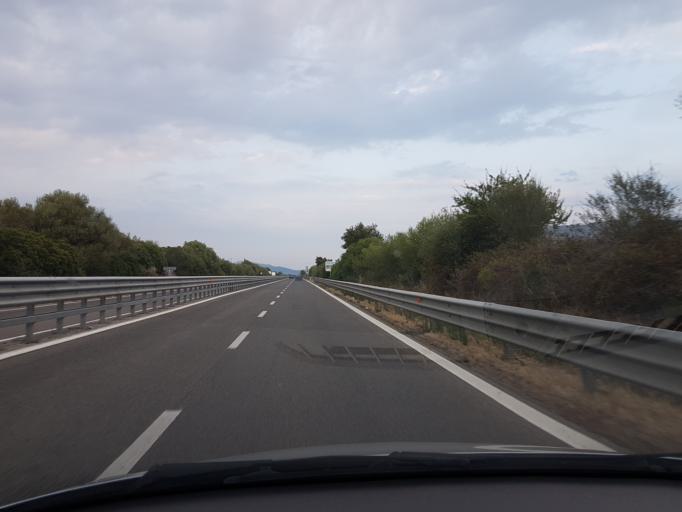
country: IT
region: Sardinia
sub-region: Provincia di Nuoro
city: Orune
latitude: 40.3754
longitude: 9.4084
